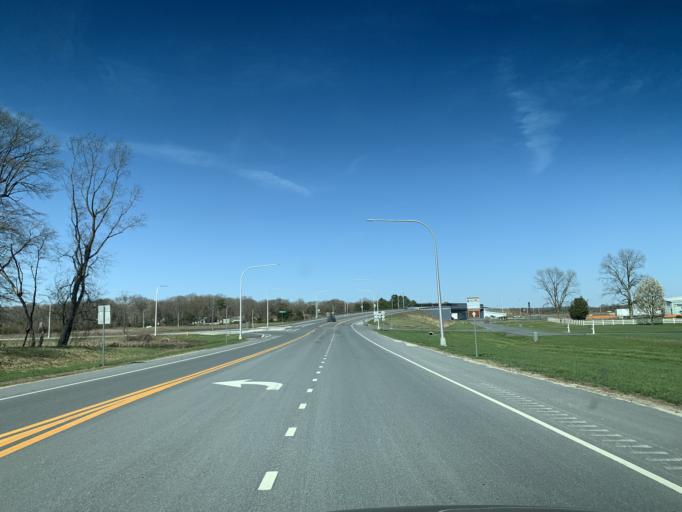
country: US
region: Delaware
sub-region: Sussex County
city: Milford
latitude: 38.9236
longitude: -75.4152
